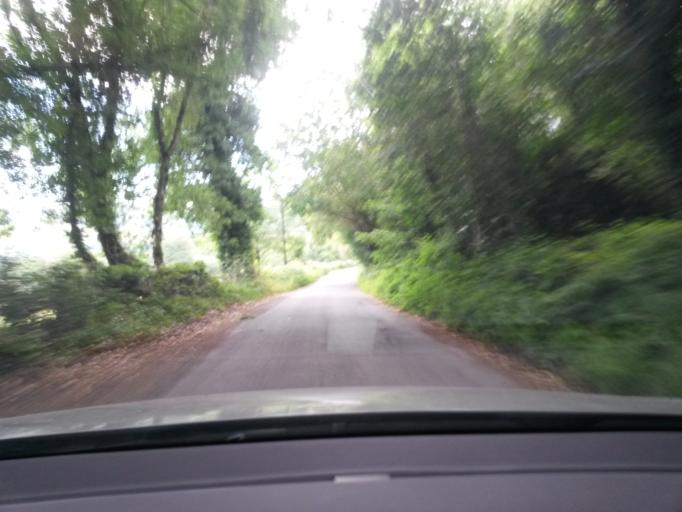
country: IE
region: Leinster
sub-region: Wicklow
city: Enniskerry
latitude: 53.1613
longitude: -6.2054
